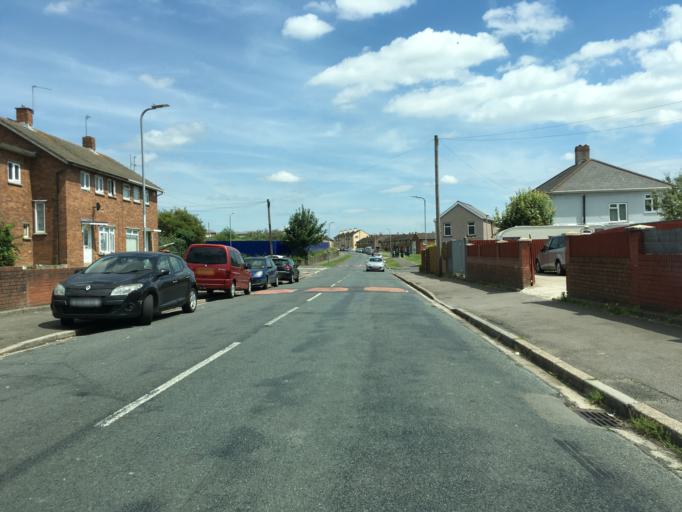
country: GB
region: Wales
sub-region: Newport
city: Caerleon
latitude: 51.5853
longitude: -2.9500
